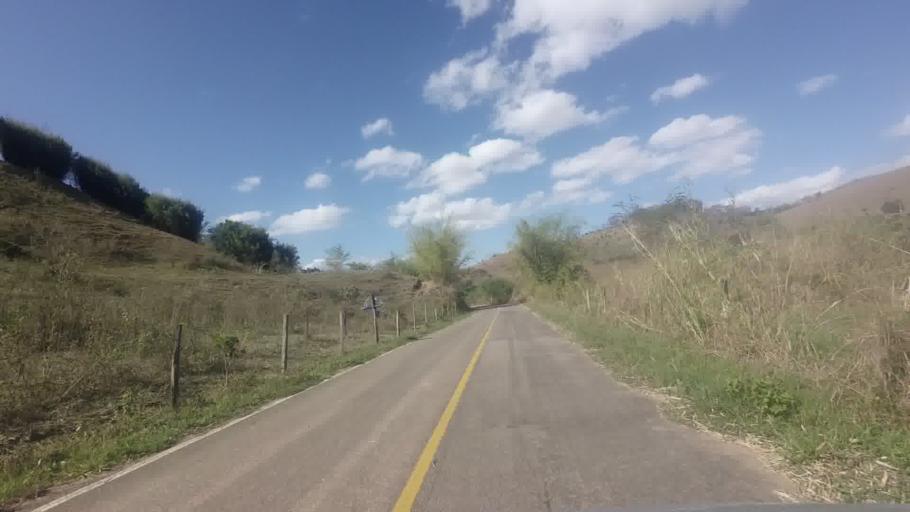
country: BR
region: Rio de Janeiro
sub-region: Bom Jesus Do Itabapoana
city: Bom Jesus do Itabapoana
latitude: -21.0943
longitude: -41.6345
